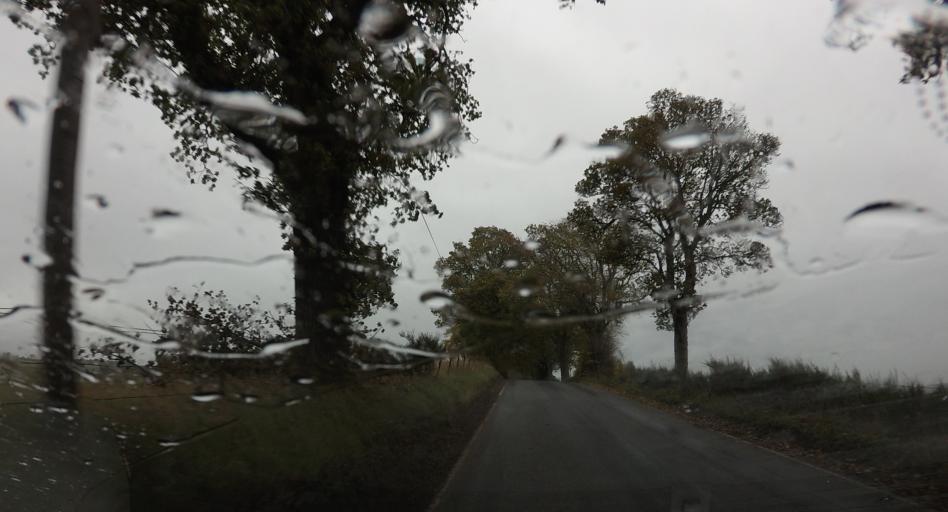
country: GB
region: Scotland
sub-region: Perth and Kinross
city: Blairgowrie
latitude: 56.5424
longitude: -3.3411
